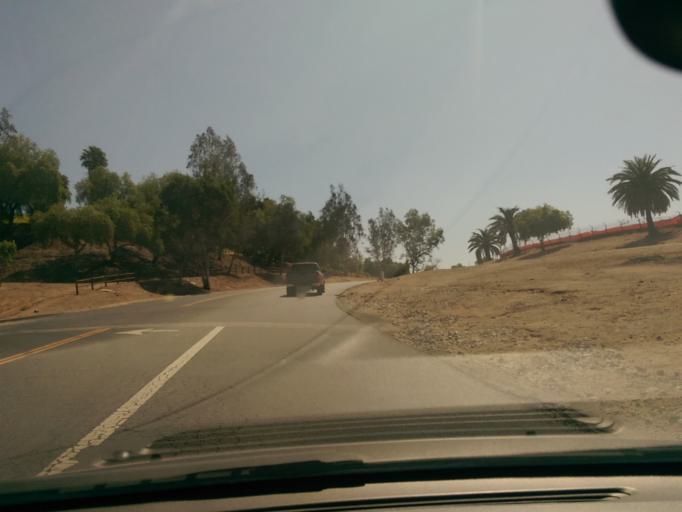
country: US
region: California
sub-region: Riverside County
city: Norco
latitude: 33.9314
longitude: -117.5653
